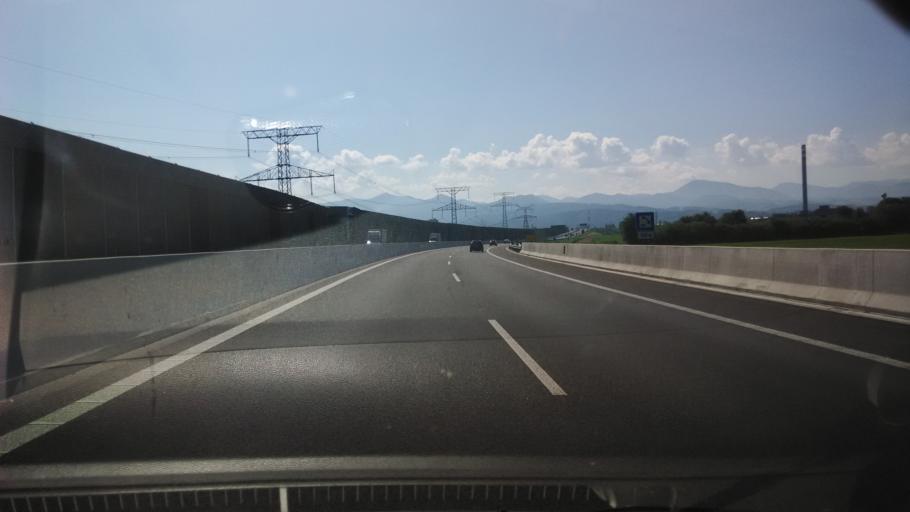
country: SK
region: Zilinsky
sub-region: Okres Zilina
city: Vrutky
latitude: 49.1203
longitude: 18.9351
